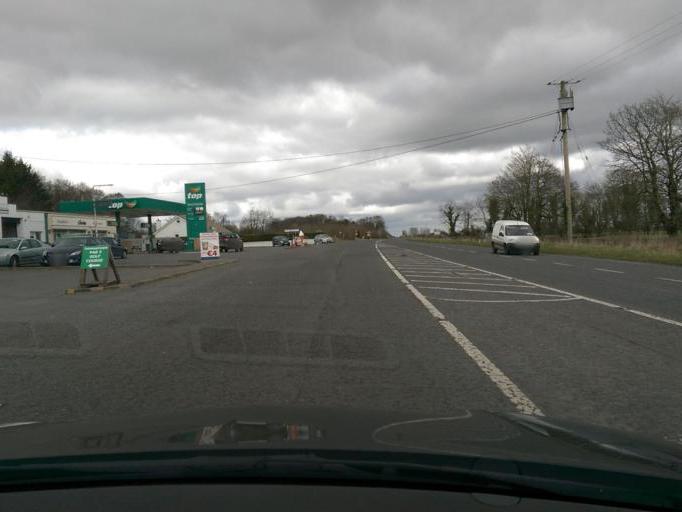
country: IE
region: Leinster
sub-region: An Iarmhi
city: Athlone
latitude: 53.3614
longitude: -8.0683
